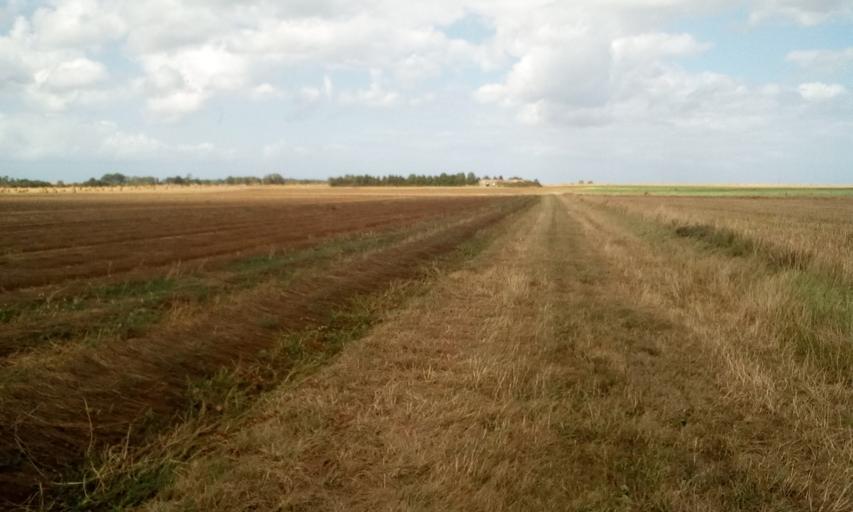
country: FR
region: Lower Normandy
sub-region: Departement du Calvados
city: Ver-sur-Mer
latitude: 49.3193
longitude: -0.5294
